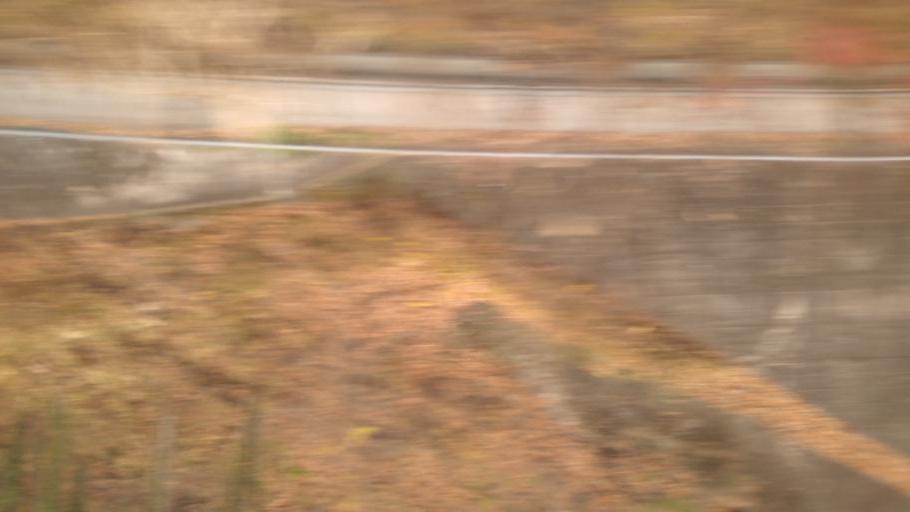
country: JP
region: Nagano
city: Hotaka
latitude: 36.3580
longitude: 137.9341
